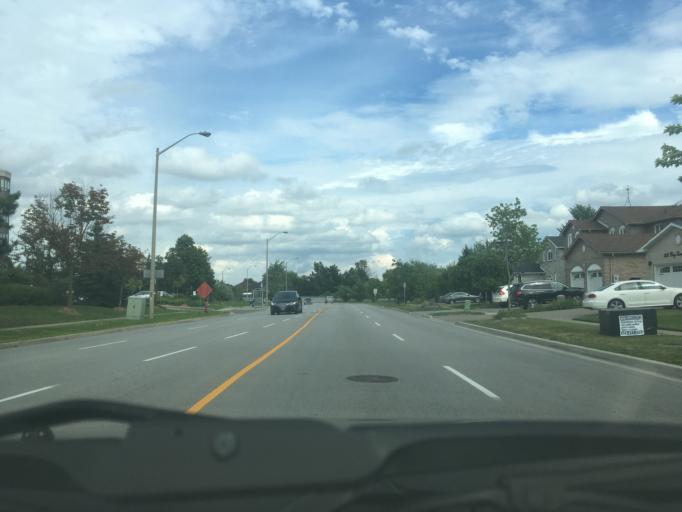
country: CA
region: Ontario
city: Brampton
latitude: 43.6532
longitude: -79.7317
